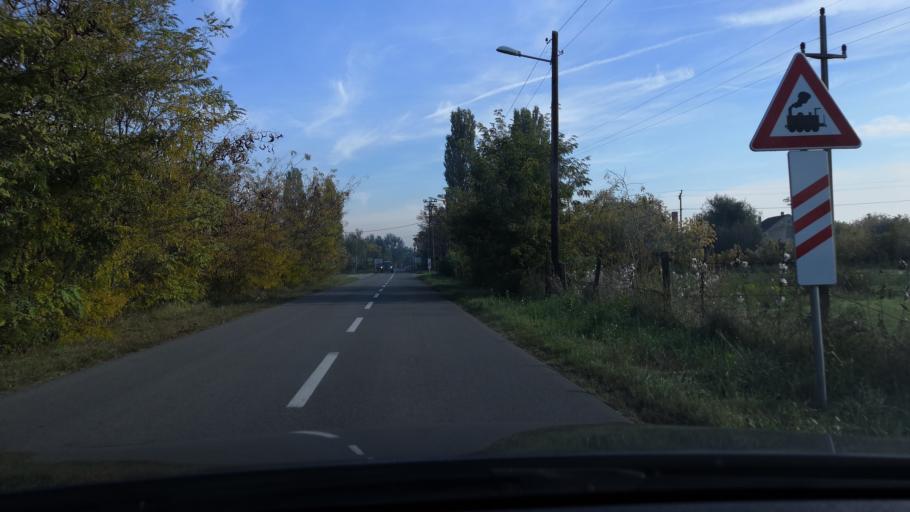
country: HU
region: Csongrad
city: Asotthalom
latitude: 46.1241
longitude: 19.8487
